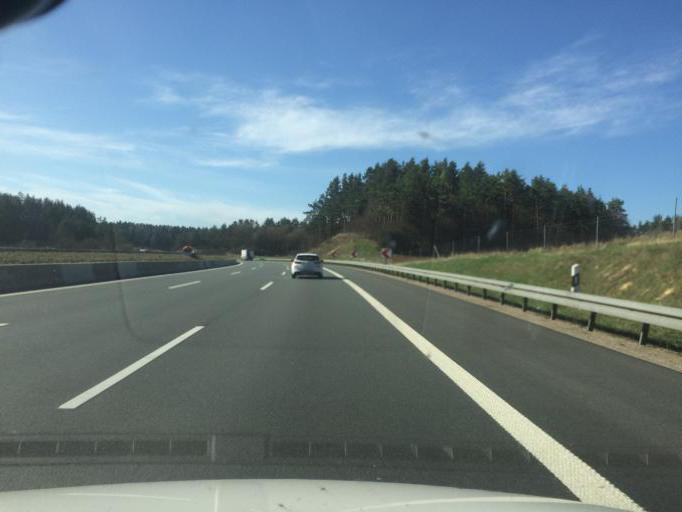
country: DE
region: Bavaria
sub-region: Upper Franconia
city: Pegnitz
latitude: 49.7699
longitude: 11.5062
